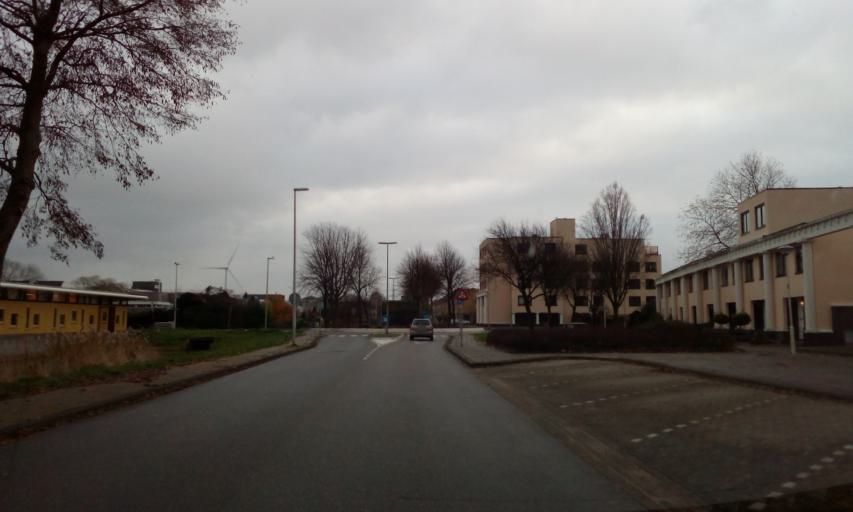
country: NL
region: South Holland
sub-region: Gemeente Zoetermeer
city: Zoetermeer
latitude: 52.0385
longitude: 4.4918
